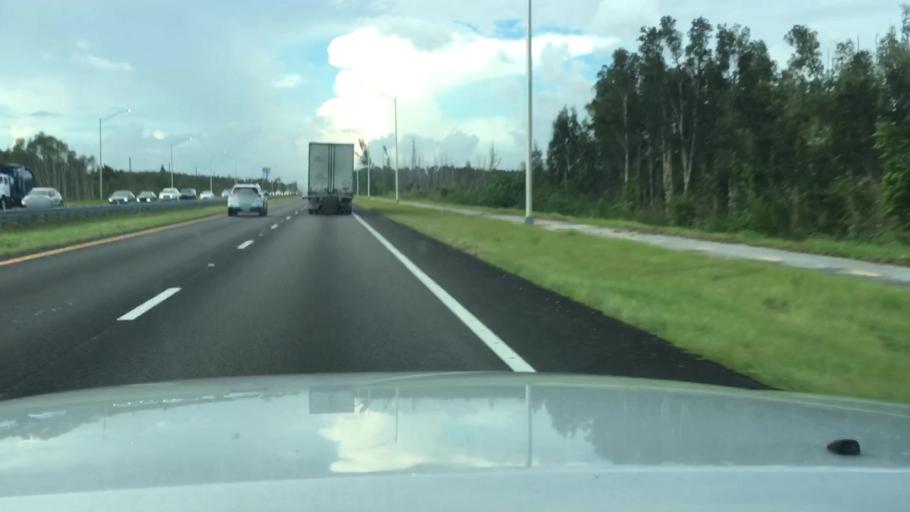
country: US
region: Florida
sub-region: Miami-Dade County
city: Kendall West
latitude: 25.7481
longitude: -80.4807
